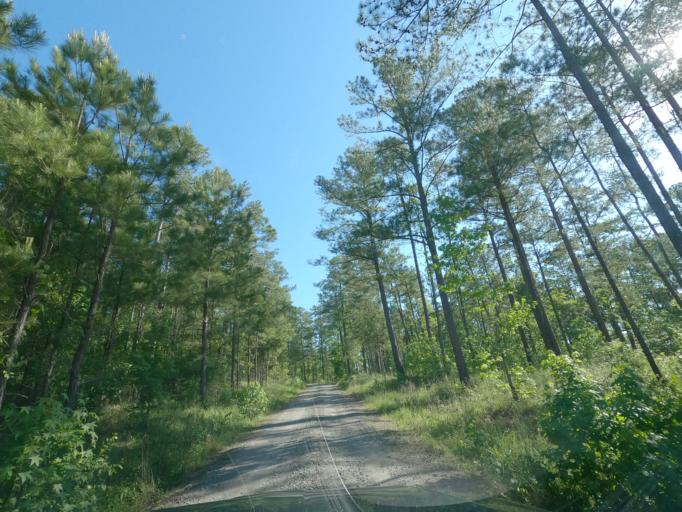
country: US
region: Georgia
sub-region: Columbia County
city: Evans
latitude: 33.6127
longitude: -82.1129
